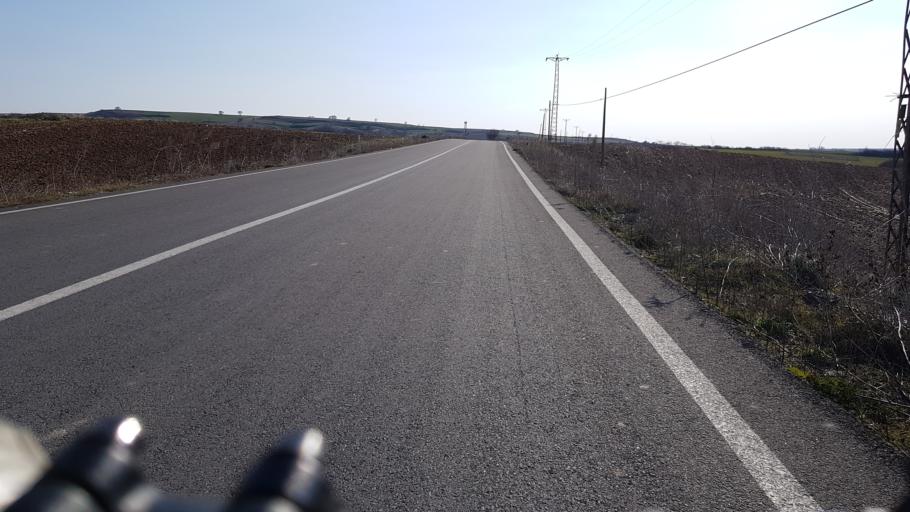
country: TR
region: Tekirdag
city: Saray
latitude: 41.3638
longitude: 27.8571
